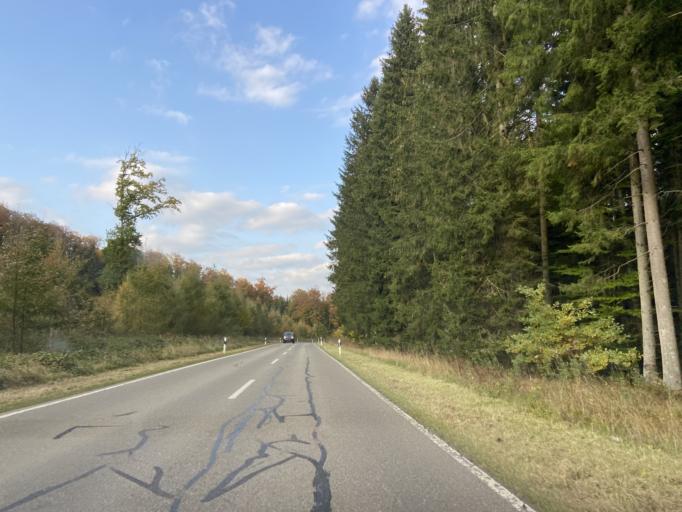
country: DE
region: Baden-Wuerttemberg
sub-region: Tuebingen Region
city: Langenenslingen
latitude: 48.1234
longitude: 9.3421
